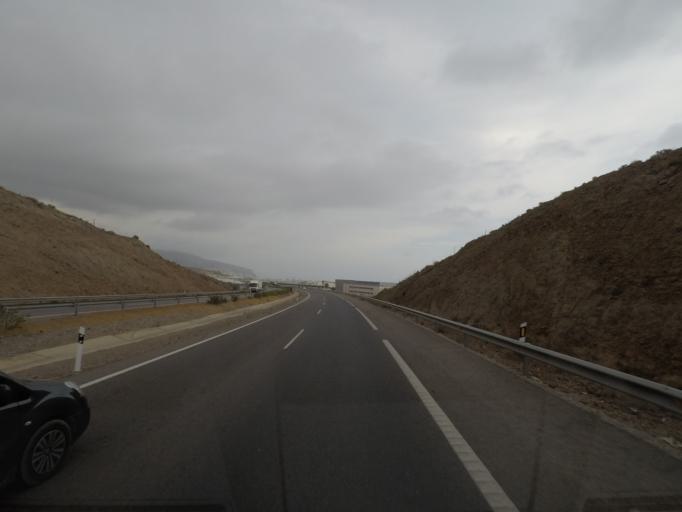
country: ES
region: Andalusia
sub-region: Provincia de Almeria
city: Vicar
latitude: 36.8108
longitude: -2.6358
